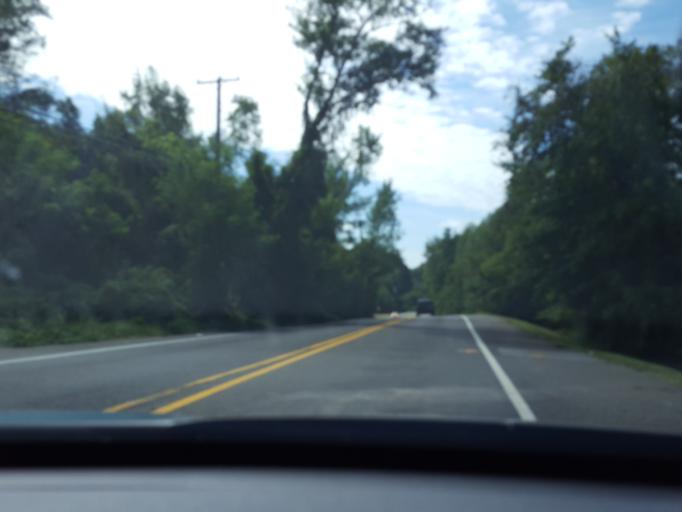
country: US
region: Maryland
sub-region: Prince George's County
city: Mellwood
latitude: 38.8037
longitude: -76.8243
